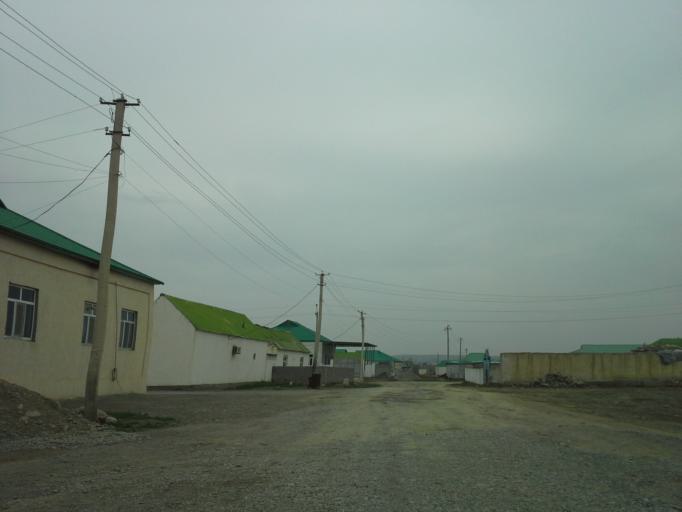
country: TM
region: Ahal
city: Abadan
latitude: 37.9810
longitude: 58.2177
